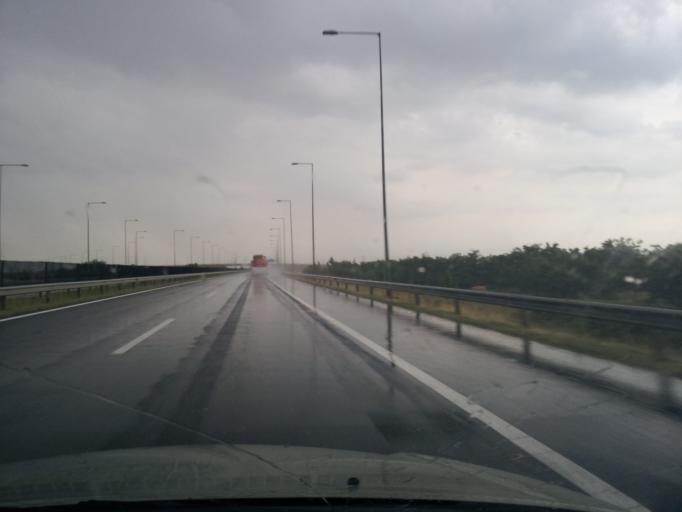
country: HU
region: Borsod-Abauj-Zemplen
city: Malyi
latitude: 48.0453
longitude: 20.8541
